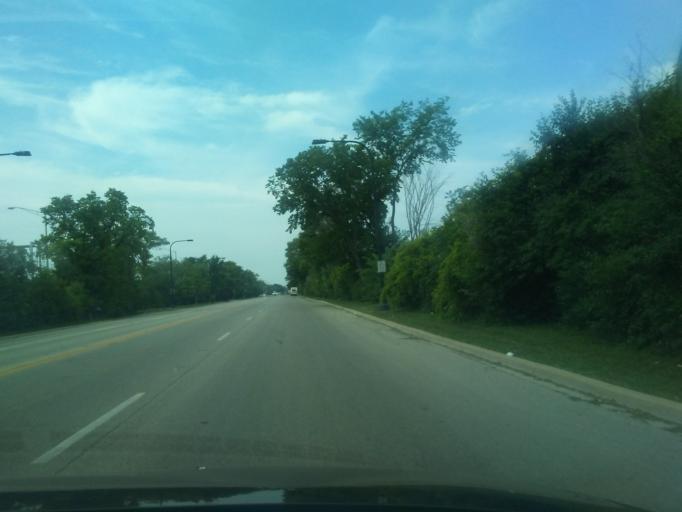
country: US
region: Illinois
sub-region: Cook County
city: Lincolnwood
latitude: 42.0058
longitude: -87.7480
